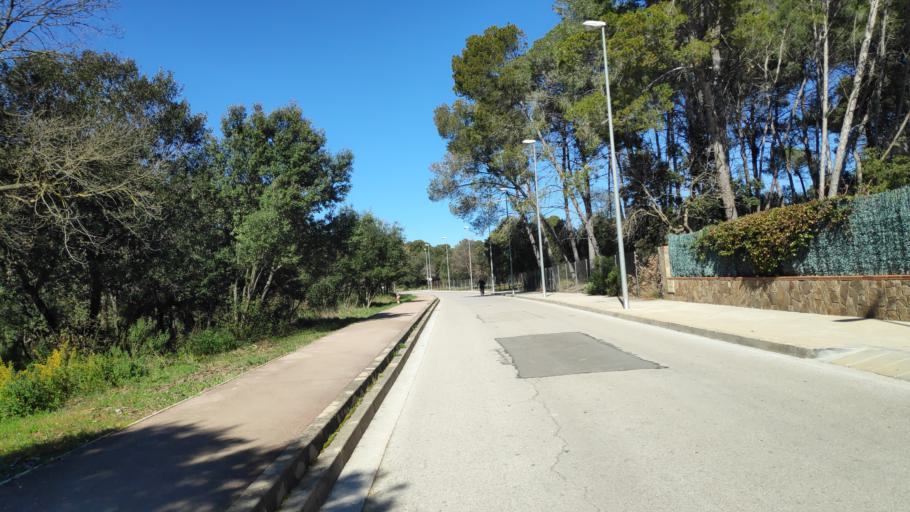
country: ES
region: Catalonia
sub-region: Provincia de Barcelona
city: Sant Quirze del Valles
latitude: 41.5620
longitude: 2.0688
